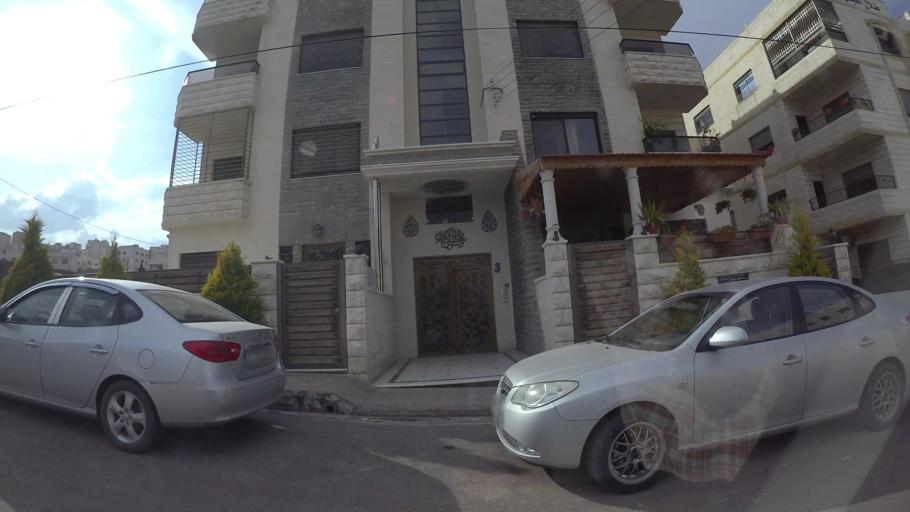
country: JO
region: Amman
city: Amman
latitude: 32.0006
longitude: 35.9489
